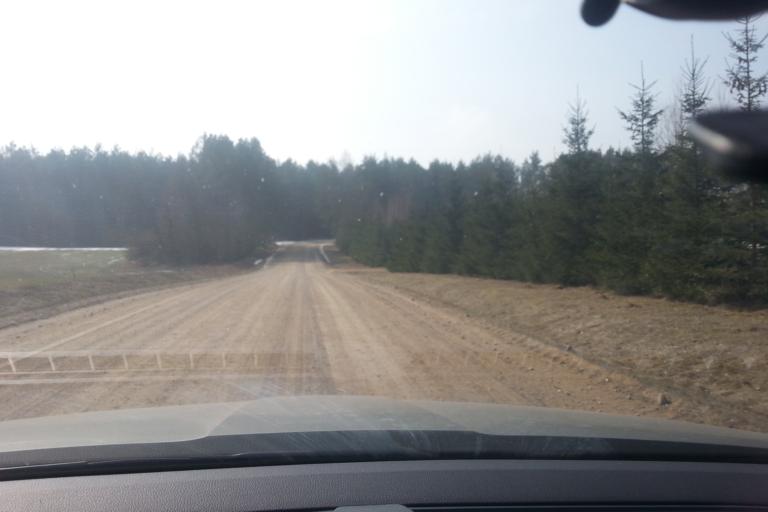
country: LT
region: Vilnius County
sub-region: Trakai
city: Rudiskes
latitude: 54.5136
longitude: 24.9360
